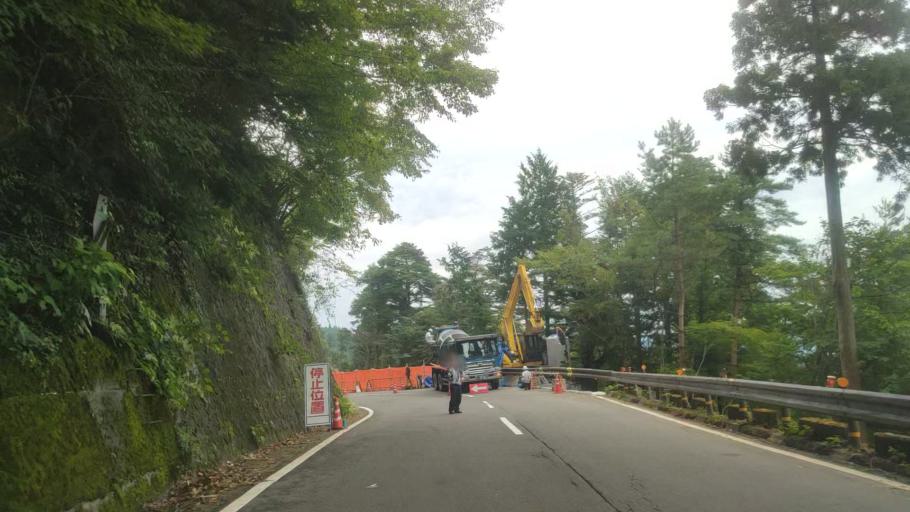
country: JP
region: Wakayama
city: Koya
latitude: 34.2158
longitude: 135.5714
